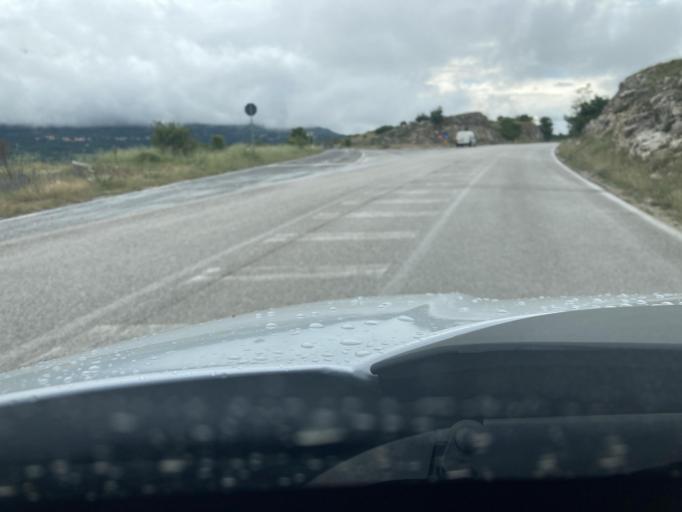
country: IT
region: Abruzzo
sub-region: Provincia dell' Aquila
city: Villa Sant'Angelo
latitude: 42.2379
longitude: 13.5286
